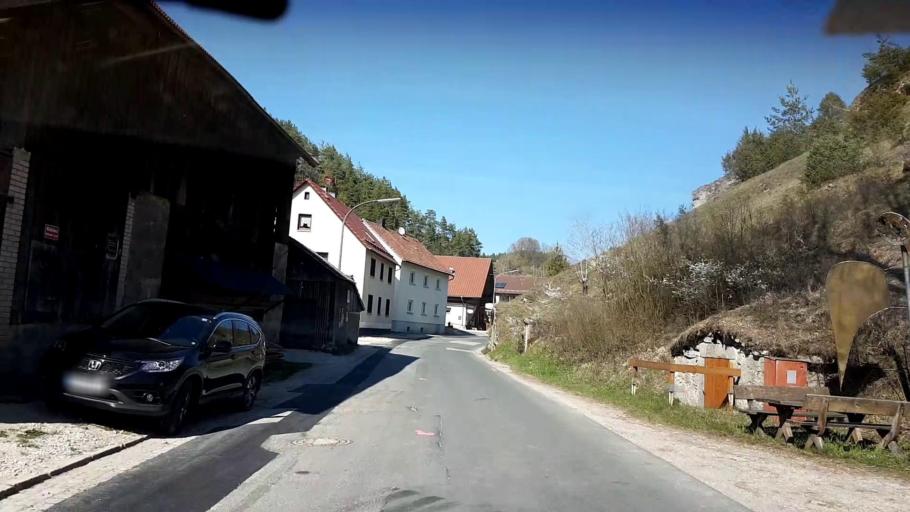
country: DE
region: Bavaria
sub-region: Upper Franconia
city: Pottenstein
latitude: 49.7860
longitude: 11.4196
